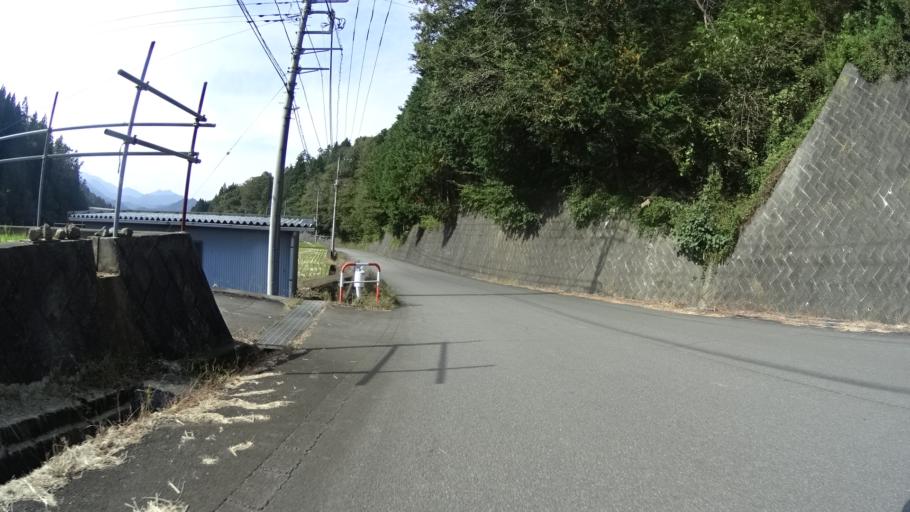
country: JP
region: Yamanashi
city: Otsuki
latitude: 35.5714
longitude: 138.9851
